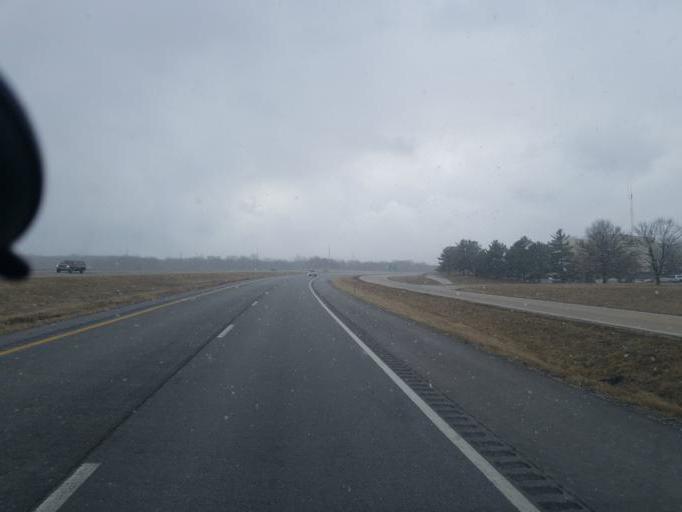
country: US
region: Missouri
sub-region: Randolph County
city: Moberly
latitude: 39.4274
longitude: -92.4133
